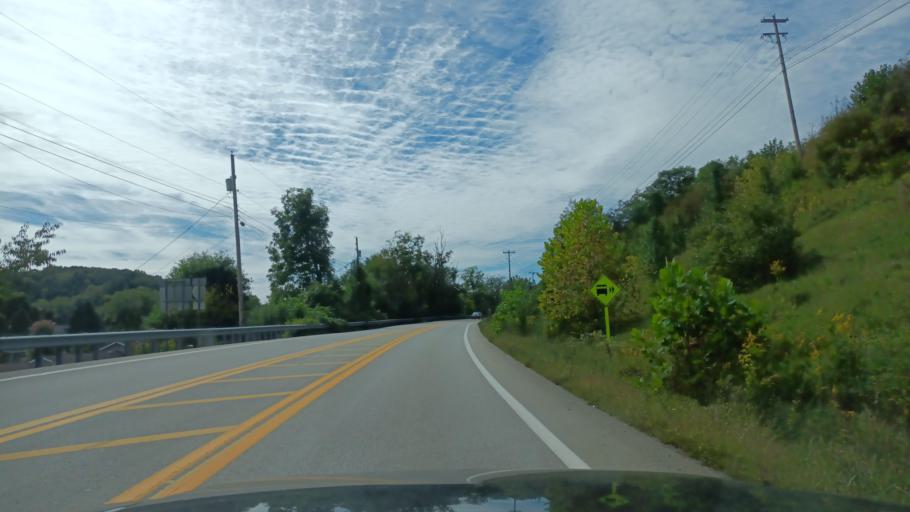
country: US
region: West Virginia
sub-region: Harrison County
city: Bridgeport
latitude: 39.2971
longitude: -80.2050
